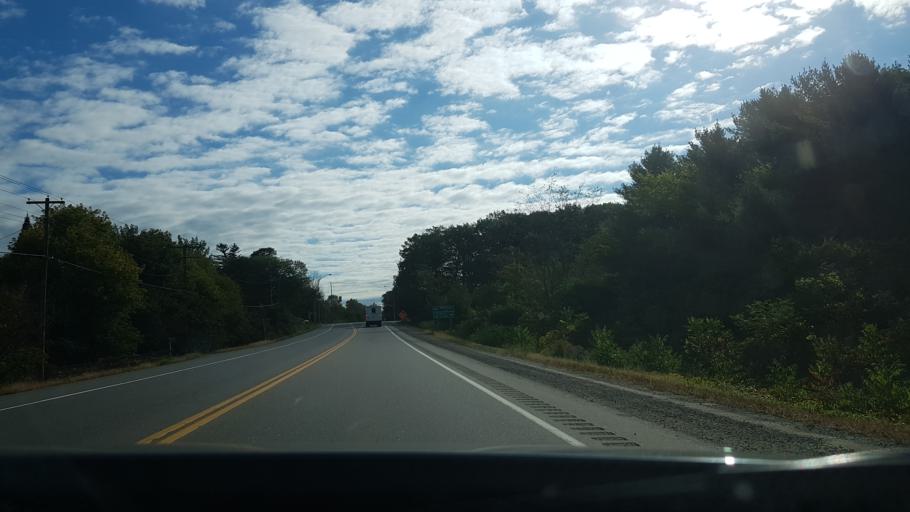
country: CA
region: Ontario
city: Orillia
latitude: 44.6143
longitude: -79.4877
